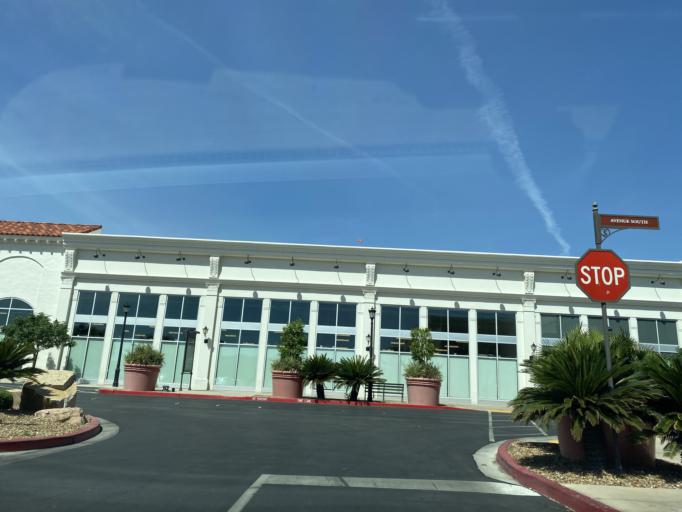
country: US
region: Nevada
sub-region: Clark County
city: Paradise
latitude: 36.0669
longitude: -115.1747
